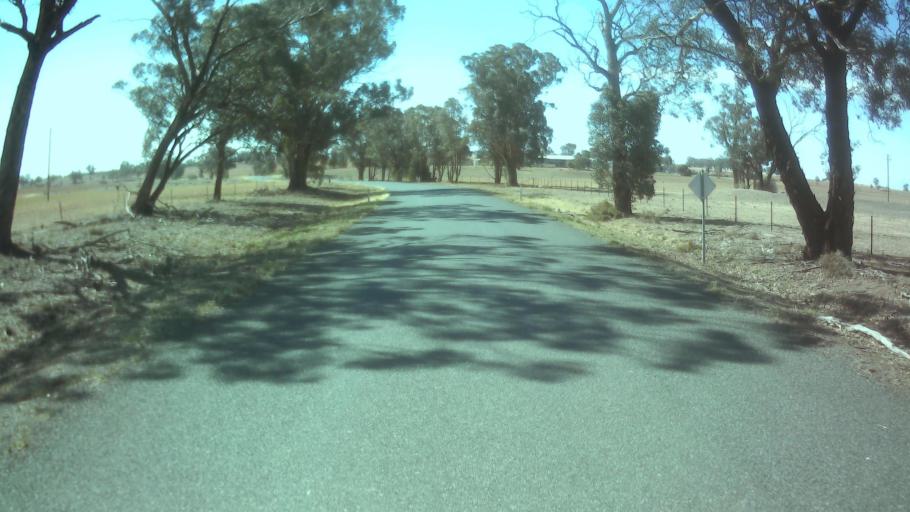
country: AU
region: New South Wales
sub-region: Weddin
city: Grenfell
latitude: -33.7648
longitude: 147.8642
